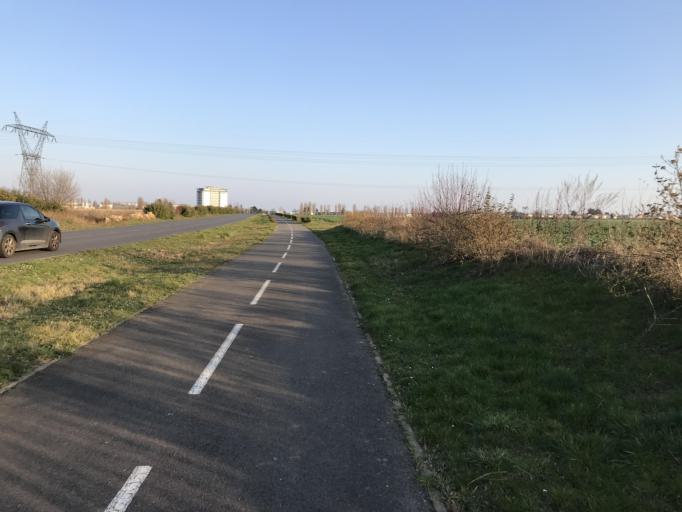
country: FR
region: Ile-de-France
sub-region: Departement de l'Essonne
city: Villejust
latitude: 48.6712
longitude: 2.2272
